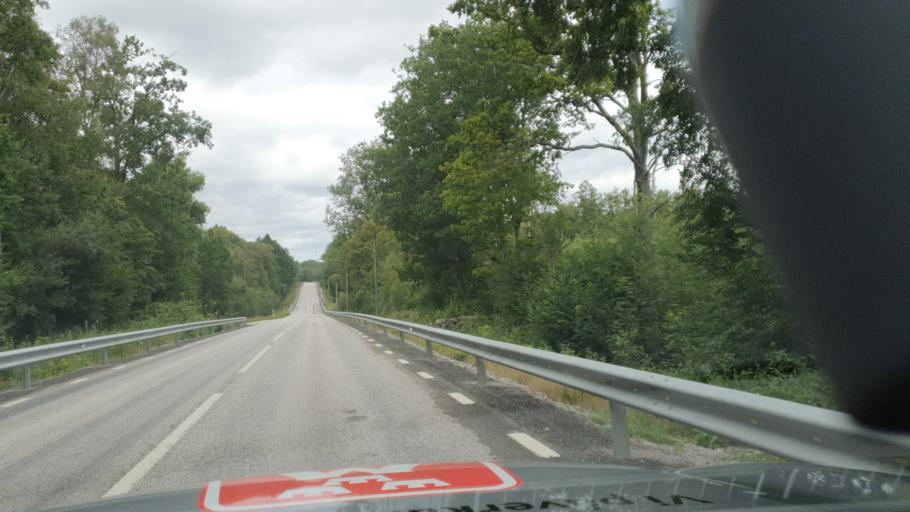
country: SE
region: Blekinge
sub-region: Karlskrona Kommun
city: Rodeby
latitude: 56.3349
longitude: 15.5745
